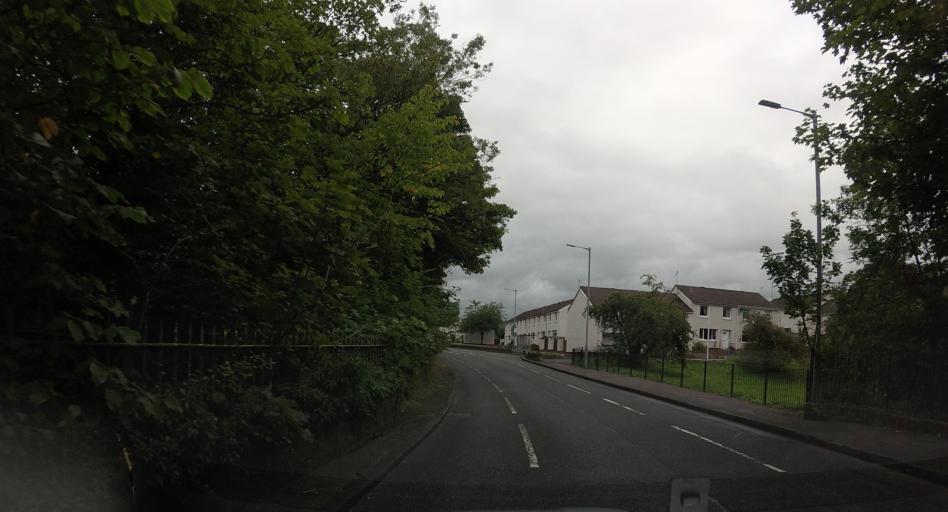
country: GB
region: Scotland
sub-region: Clackmannanshire
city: Clackmannan
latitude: 56.1110
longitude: -3.7568
